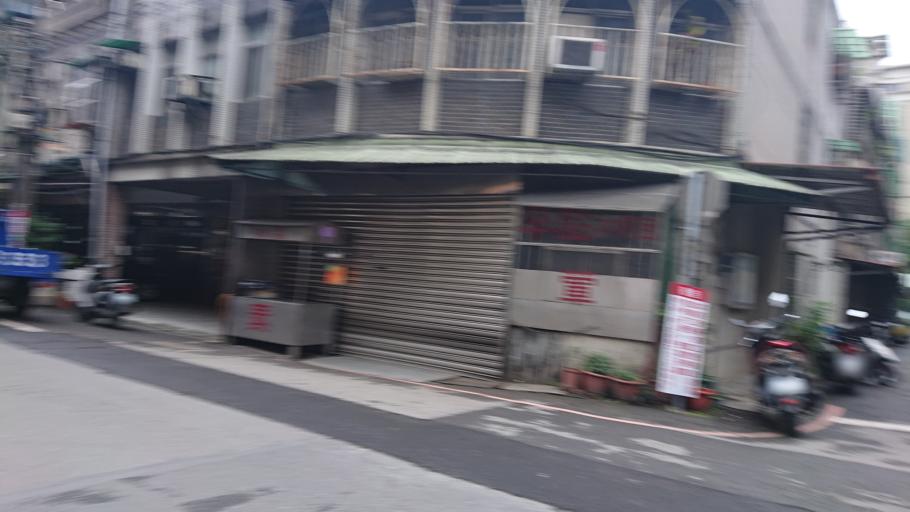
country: TW
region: Taiwan
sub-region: Taoyuan
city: Taoyuan
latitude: 24.9363
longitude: 121.3671
